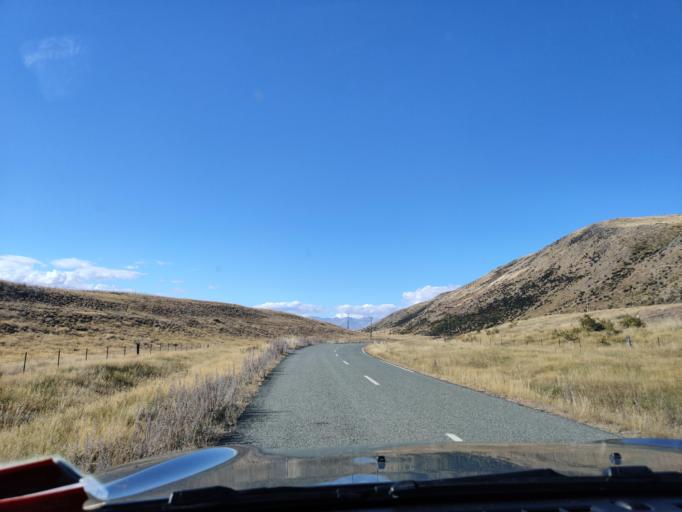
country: NZ
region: Canterbury
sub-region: Timaru District
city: Pleasant Point
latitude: -43.9901
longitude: 170.4504
